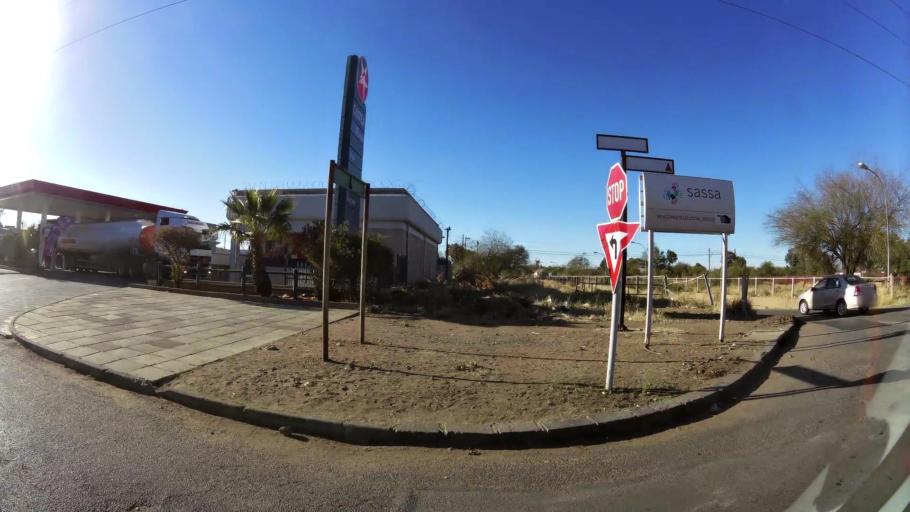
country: ZA
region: Northern Cape
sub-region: Frances Baard District Municipality
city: Kimberley
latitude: -28.7585
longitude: 24.7856
